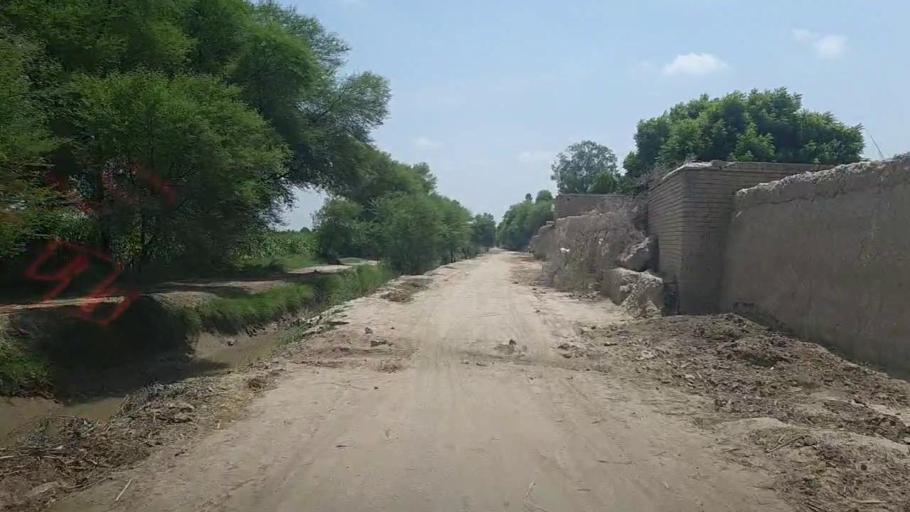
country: PK
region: Sindh
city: Ubauro
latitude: 28.2786
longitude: 69.8090
